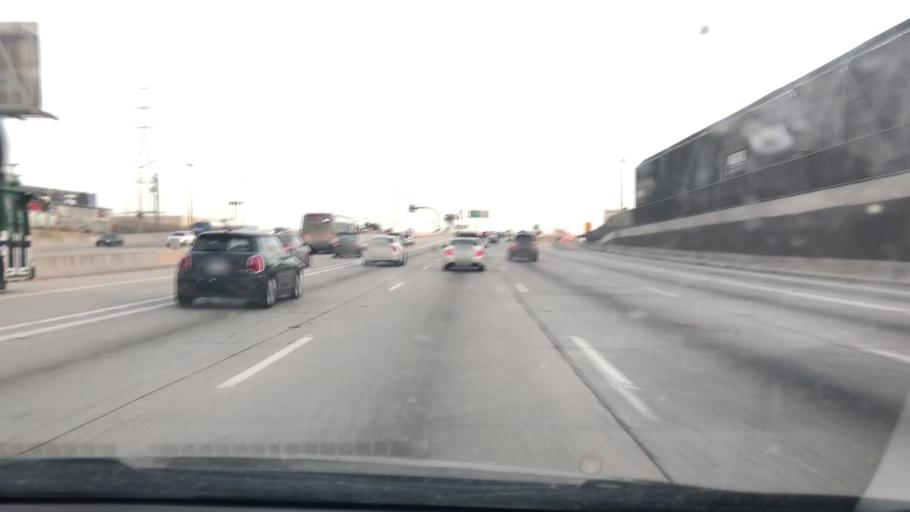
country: US
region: California
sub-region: Los Angeles County
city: West Rancho Dominguez
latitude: 33.8960
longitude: -118.2864
